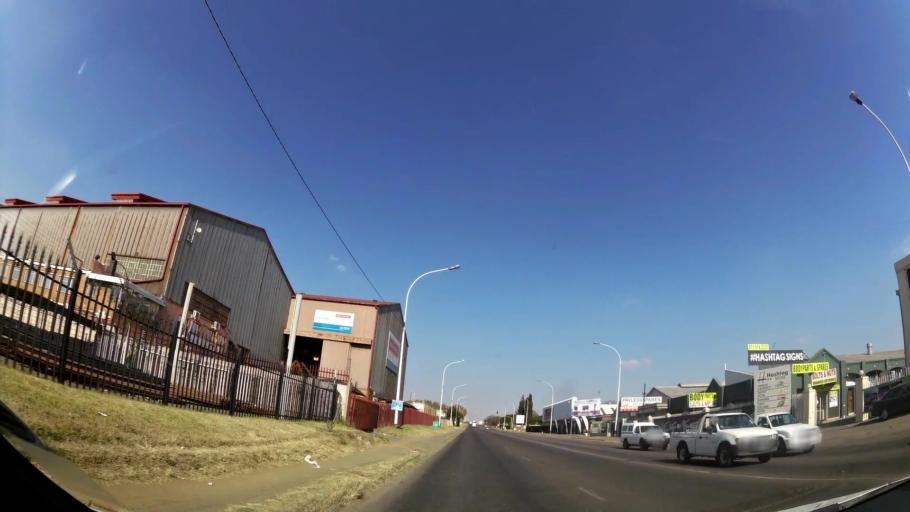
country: ZA
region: Gauteng
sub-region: Ekurhuleni Metropolitan Municipality
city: Boksburg
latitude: -26.2176
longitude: 28.2887
